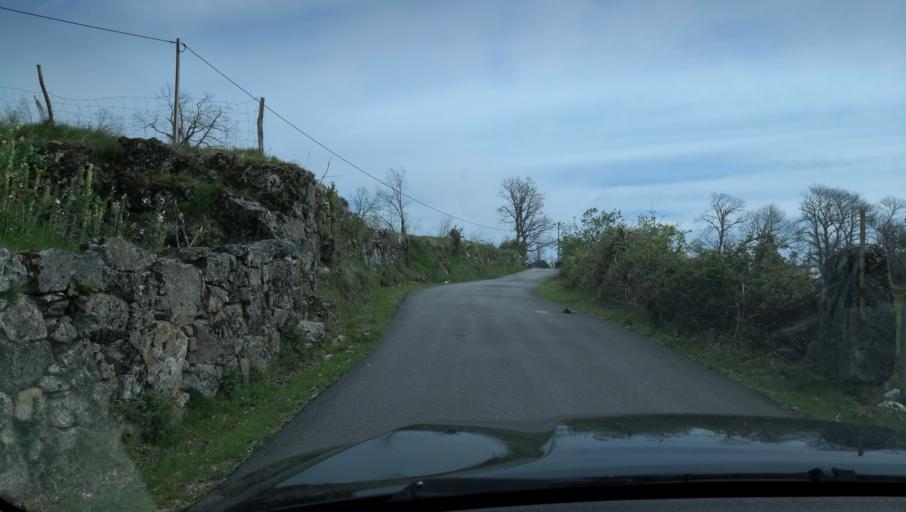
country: PT
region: Vila Real
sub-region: Vila Real
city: Vila Real
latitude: 41.2961
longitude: -7.8282
